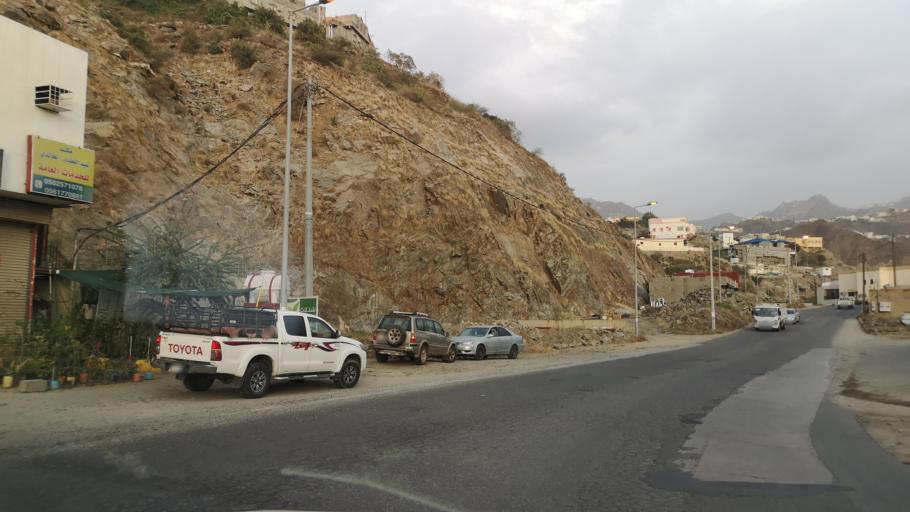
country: YE
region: Sa'dah
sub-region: Monabbih
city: Suq al Khamis
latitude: 17.3469
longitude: 43.1462
